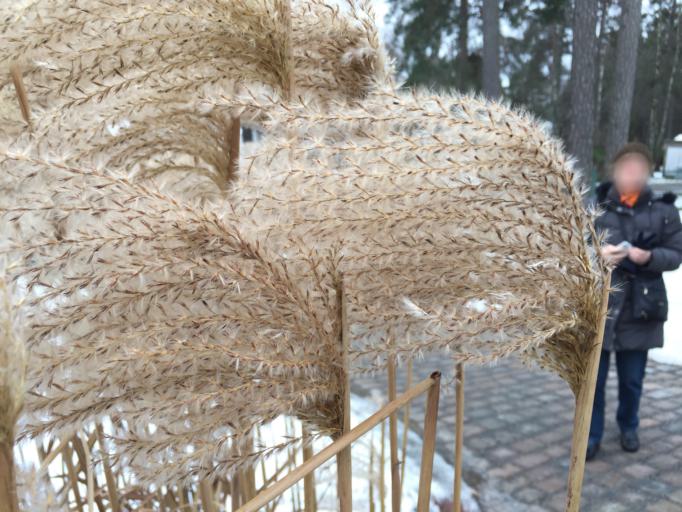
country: SE
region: Stockholm
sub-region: Haninge Kommun
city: Jordbro
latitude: 59.1244
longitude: 18.1093
